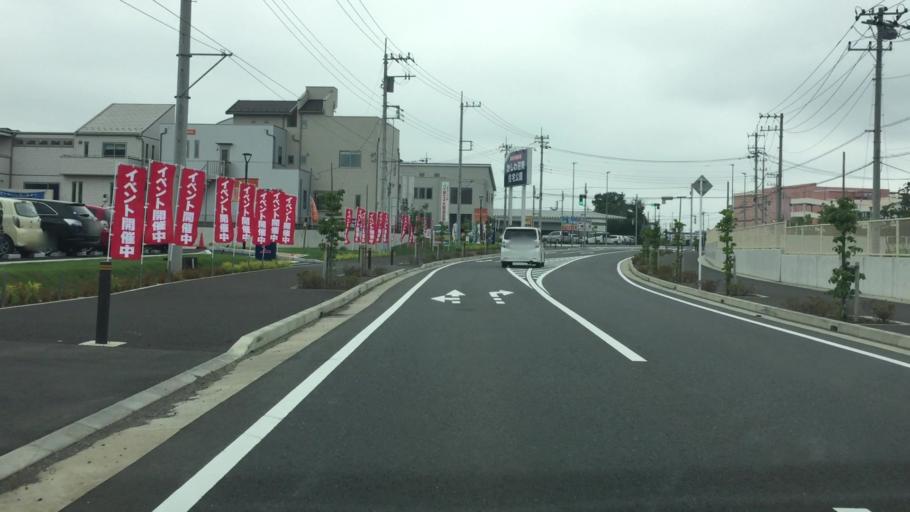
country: JP
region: Chiba
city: Abiko
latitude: 35.8351
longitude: 140.0161
